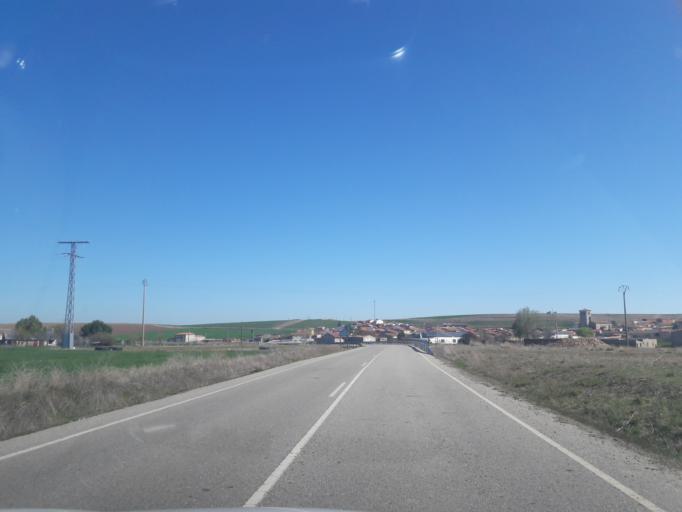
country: ES
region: Castille and Leon
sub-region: Provincia de Salamanca
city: Mancera de Abajo
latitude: 40.8360
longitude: -5.2033
